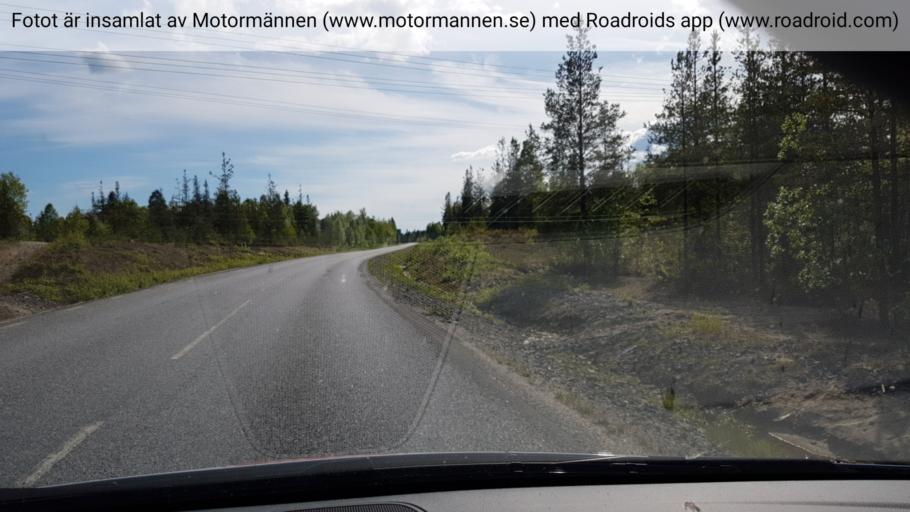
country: SE
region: Vaesterbotten
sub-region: Umea Kommun
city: Saevar
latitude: 63.9178
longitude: 20.5396
